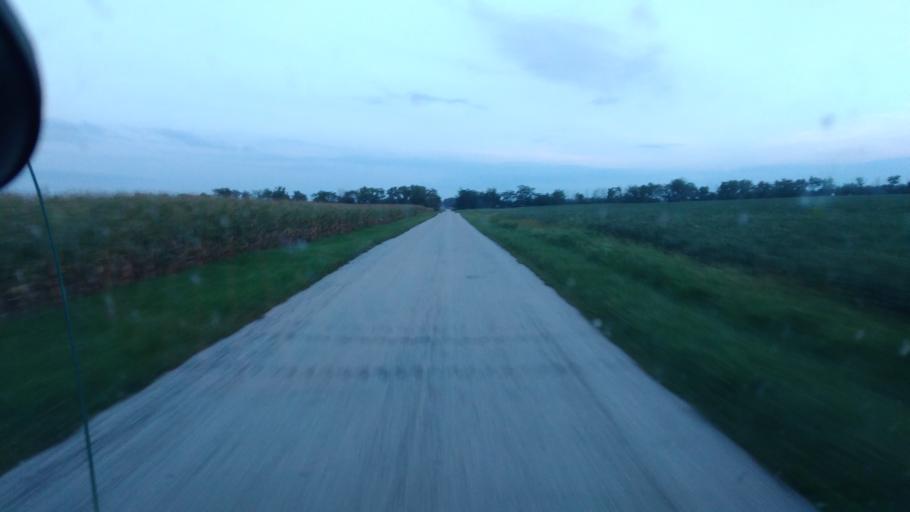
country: US
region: Ohio
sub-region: Hardin County
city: Forest
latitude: 40.6693
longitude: -83.4595
